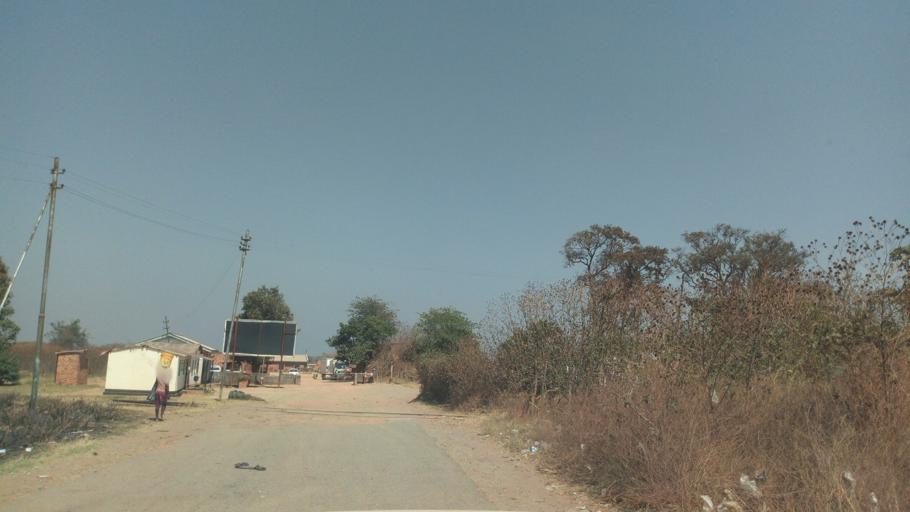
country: CD
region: Katanga
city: Kipushi
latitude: -11.7623
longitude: 27.2290
